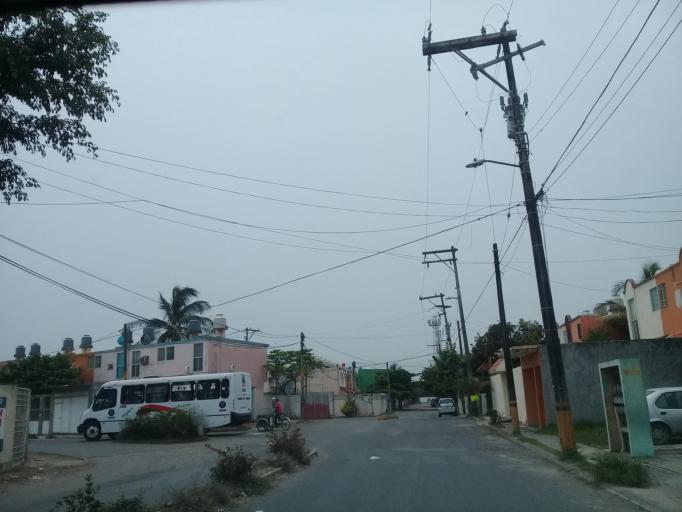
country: MX
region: Veracruz
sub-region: Veracruz
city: Las Amapolas
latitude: 19.1531
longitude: -96.2041
